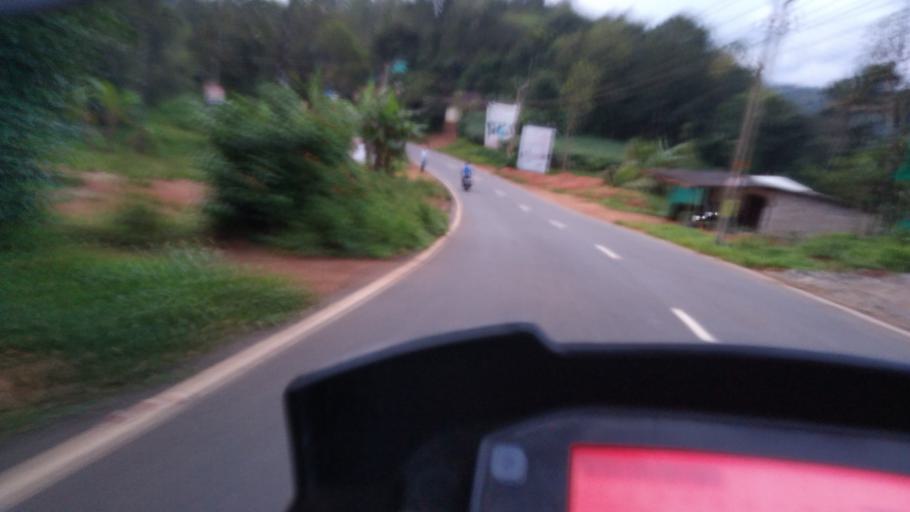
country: IN
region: Kerala
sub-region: Idukki
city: Munnar
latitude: 9.9685
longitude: 77.1336
